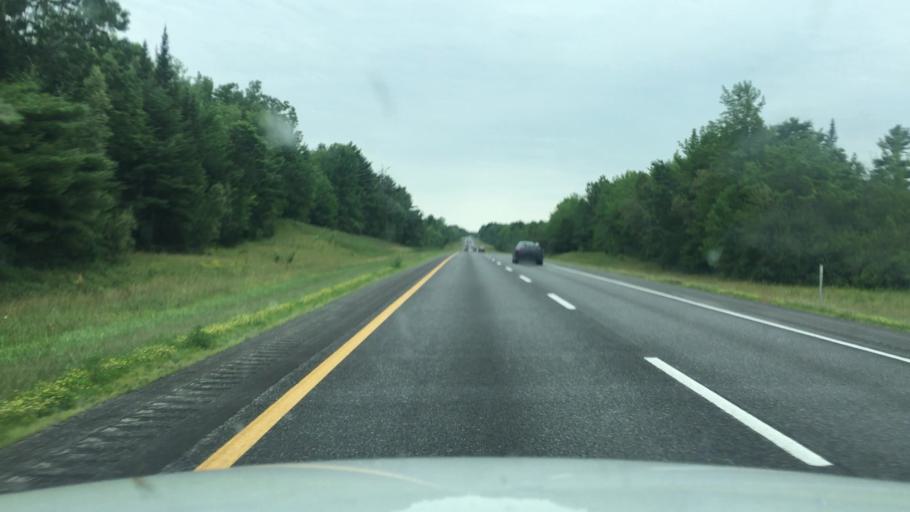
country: US
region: Maine
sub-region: Sagadahoc County
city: Richmond
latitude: 44.1431
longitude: -69.8422
